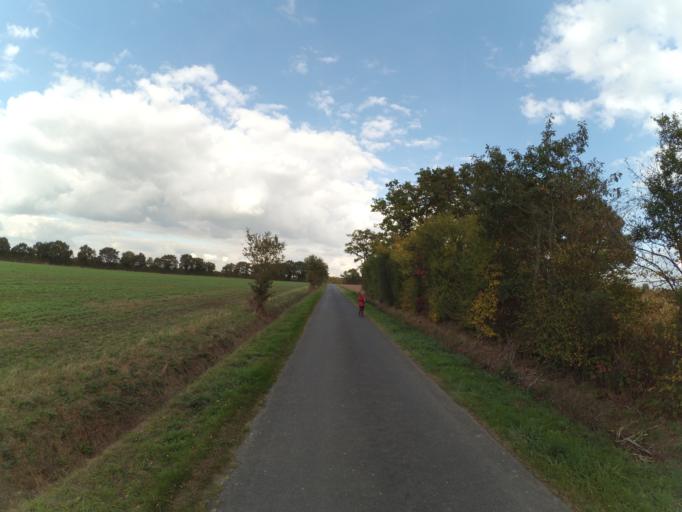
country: FR
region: Pays de la Loire
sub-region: Departement de la Loire-Atlantique
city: Saint-Lumine-de-Clisson
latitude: 47.0676
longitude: -1.3355
